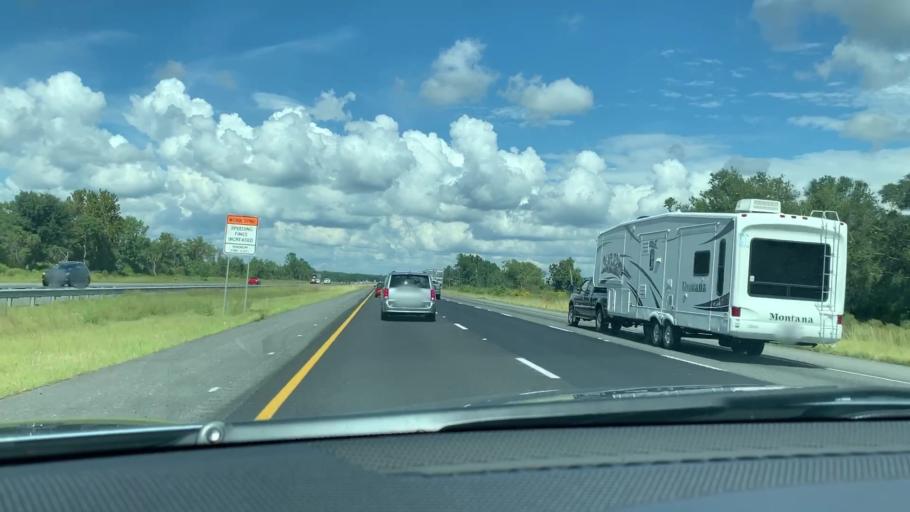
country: US
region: Georgia
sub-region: Camden County
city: Woodbine
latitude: 31.0247
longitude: -81.6566
